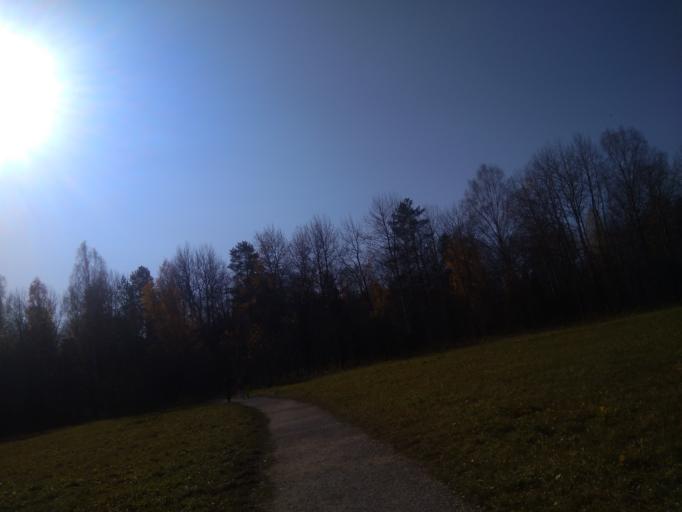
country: RU
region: Sverdlovsk
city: Mikhaylovsk
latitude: 56.5222
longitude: 59.2350
